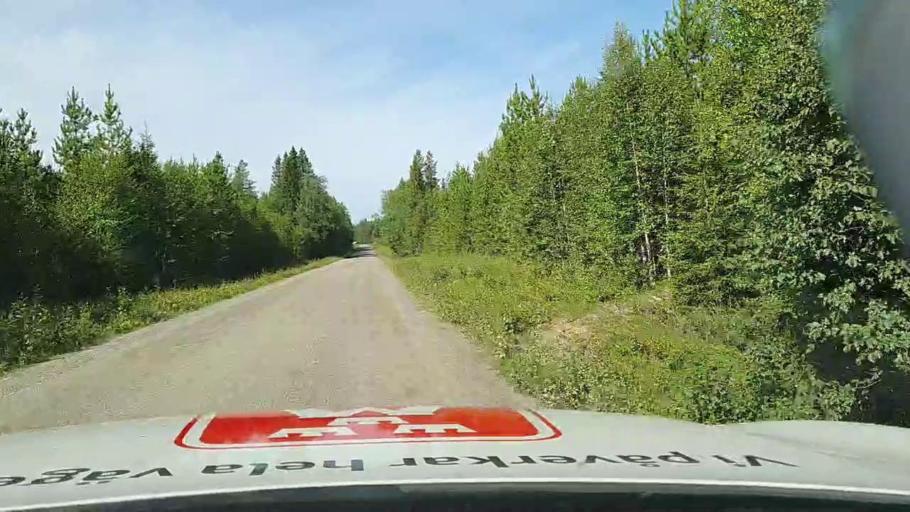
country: SE
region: Jaemtland
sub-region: Stroemsunds Kommun
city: Stroemsund
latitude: 63.7251
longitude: 15.2610
